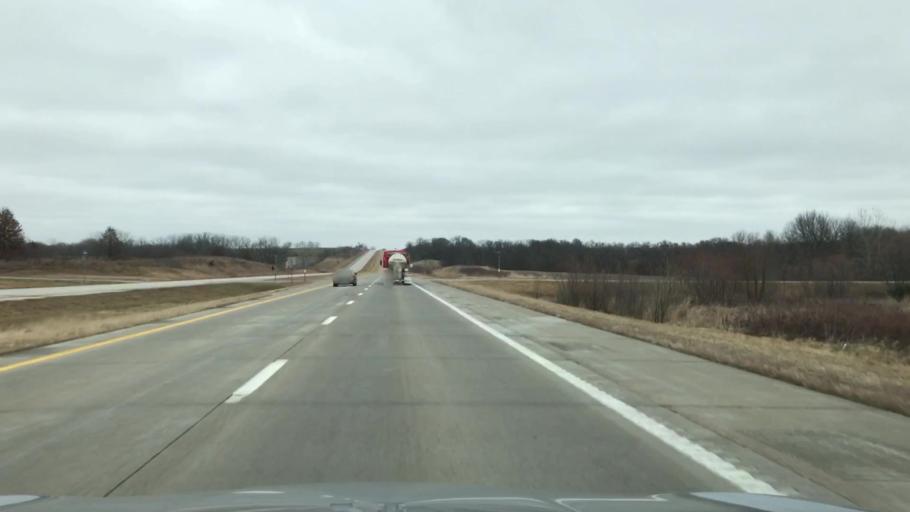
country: US
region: Missouri
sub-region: Caldwell County
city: Hamilton
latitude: 39.7349
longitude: -93.9465
